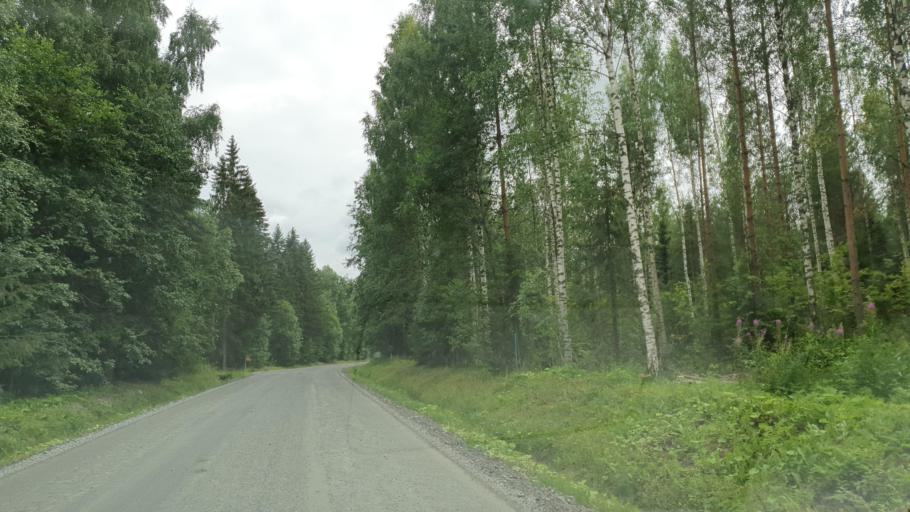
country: FI
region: Northern Savo
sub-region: Ylae-Savo
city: Iisalmi
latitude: 63.5322
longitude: 27.0883
